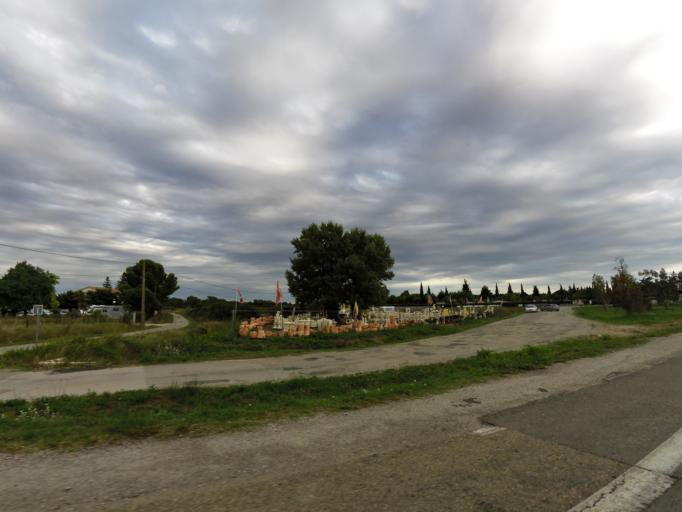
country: FR
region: Languedoc-Roussillon
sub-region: Departement du Gard
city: Aimargues
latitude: 43.6830
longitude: 4.2149
